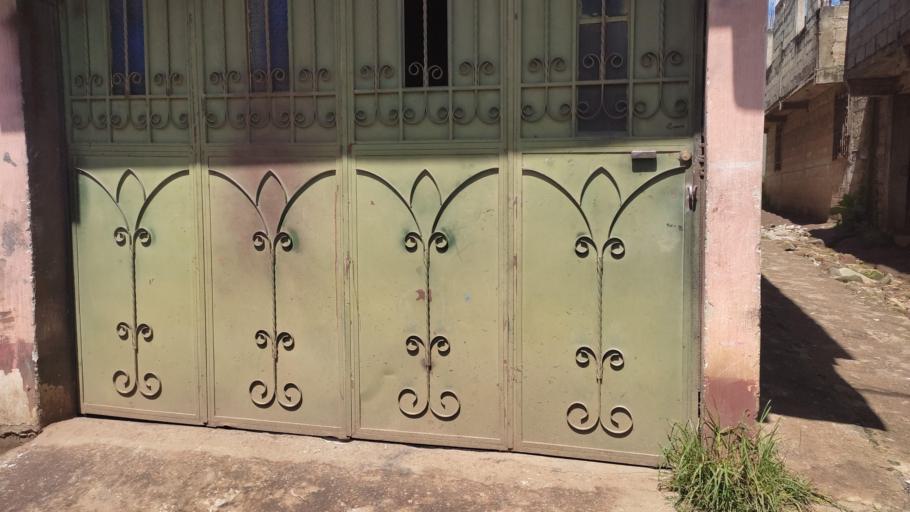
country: GT
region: Quetzaltenango
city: Quetzaltenango
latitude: 14.8573
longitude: -91.5257
